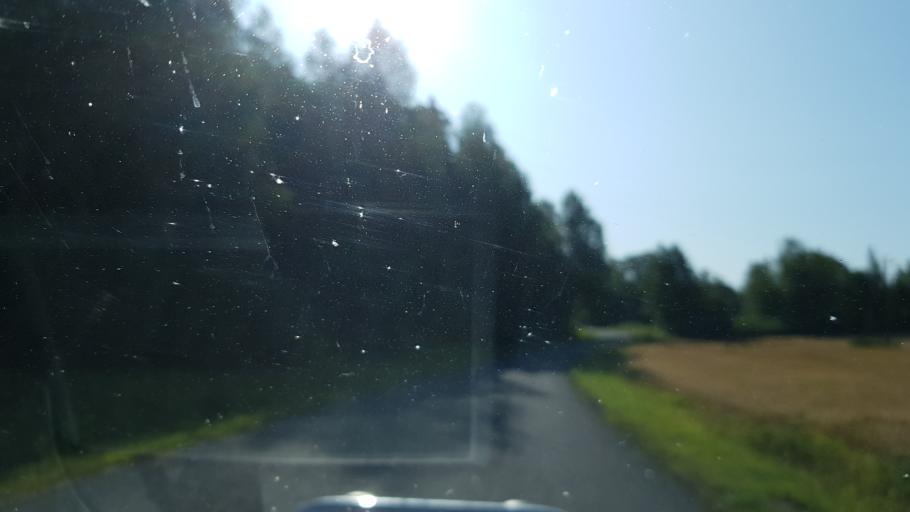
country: LV
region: Apes Novads
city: Ape
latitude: 57.6583
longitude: 26.7102
